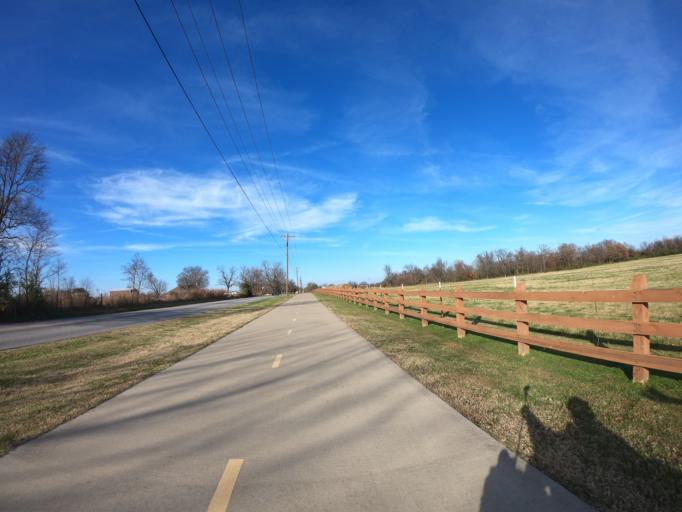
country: US
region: Arkansas
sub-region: Benton County
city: Lowell
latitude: 36.2625
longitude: -94.1547
